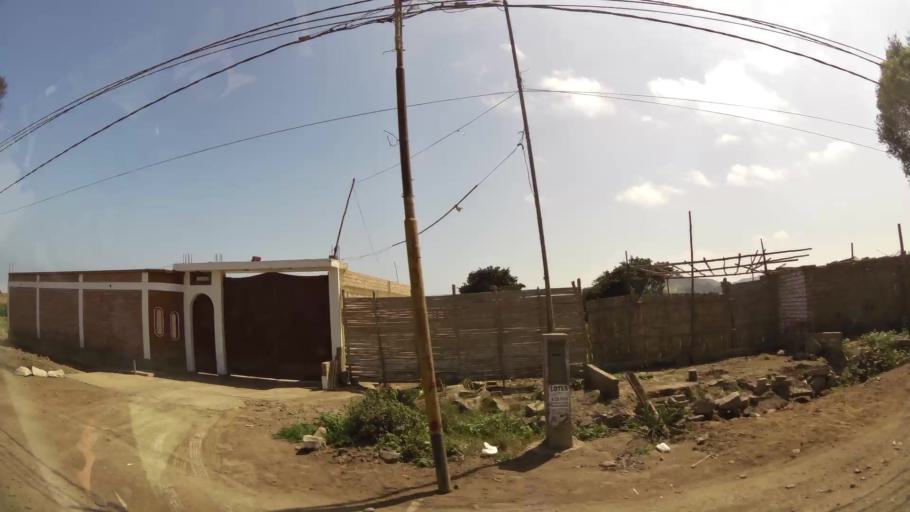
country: PE
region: Lima
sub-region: Provincia de Canete
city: Mala
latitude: -12.6730
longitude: -76.6475
